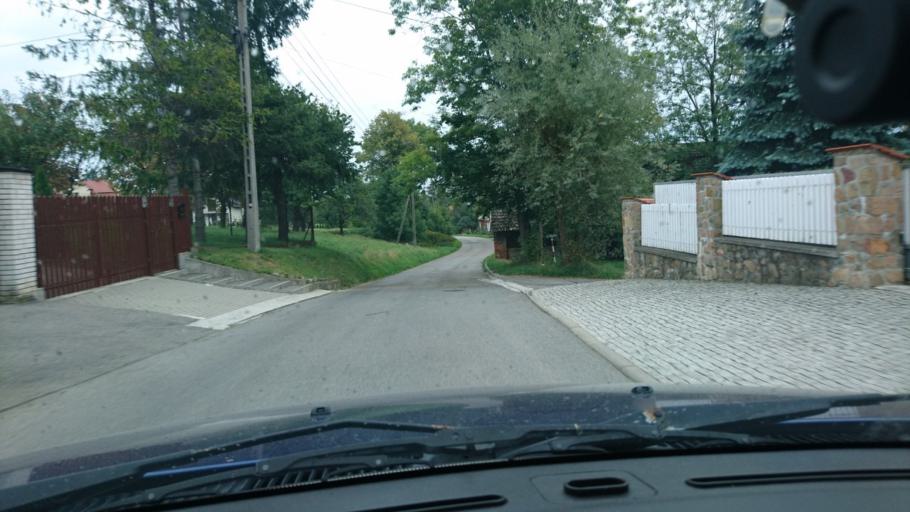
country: PL
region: Silesian Voivodeship
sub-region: Bielsko-Biala
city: Bielsko-Biala
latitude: 49.8258
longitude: 19.0064
